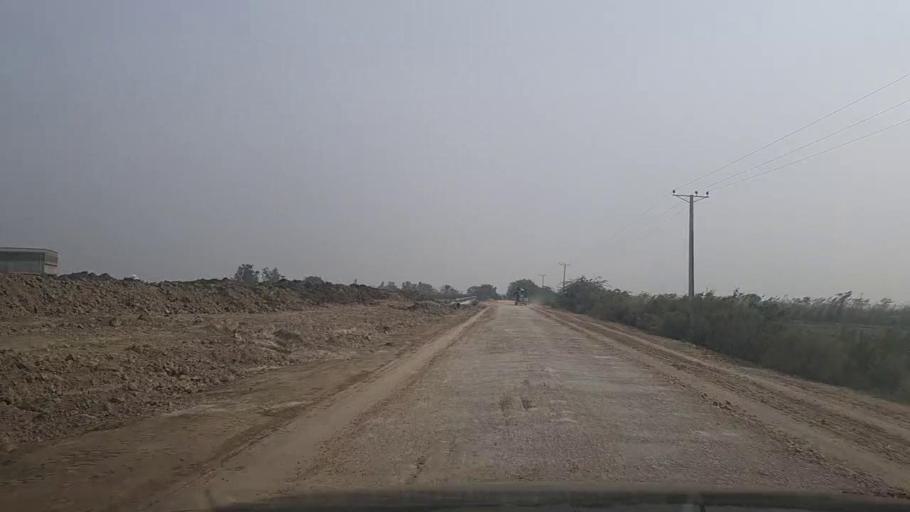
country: PK
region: Sindh
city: Mirpur Sakro
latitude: 24.4745
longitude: 67.6675
